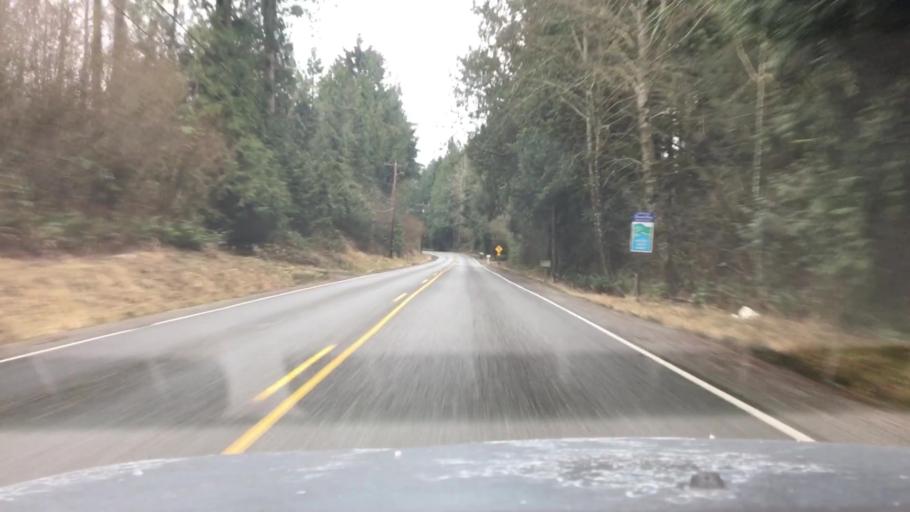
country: US
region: Washington
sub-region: Whatcom County
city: Sudden Valley
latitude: 48.6441
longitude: -122.3226
